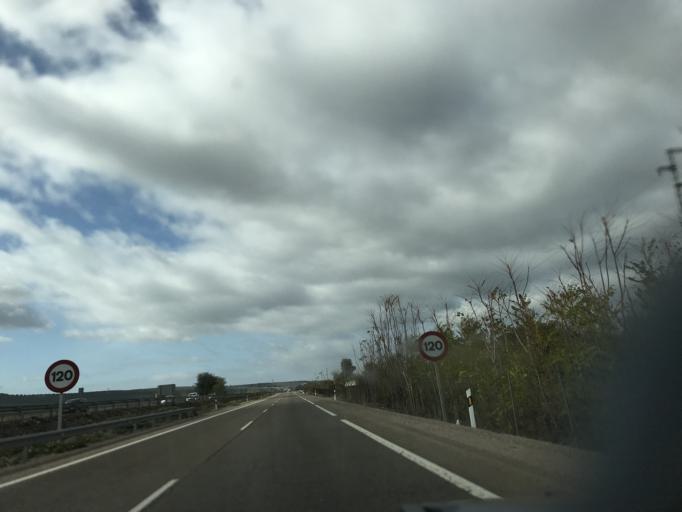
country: ES
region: Andalusia
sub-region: Provincia de Jaen
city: Andujar
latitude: 38.0317
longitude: -4.0841
